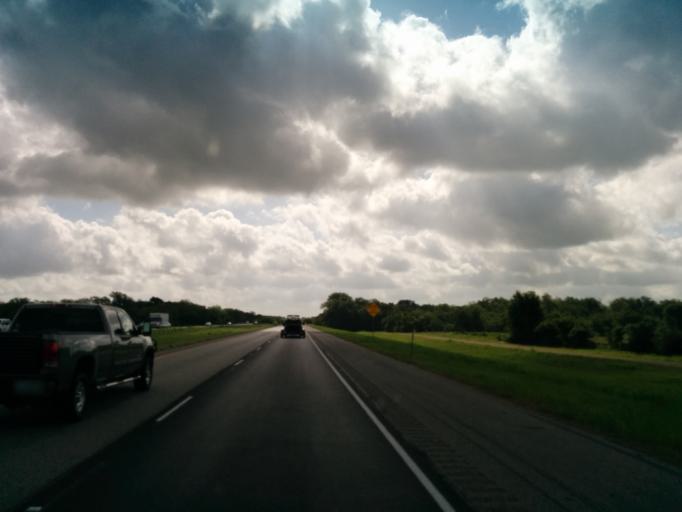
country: US
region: Texas
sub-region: Gonzales County
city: Waelder
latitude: 29.6622
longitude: -97.3860
